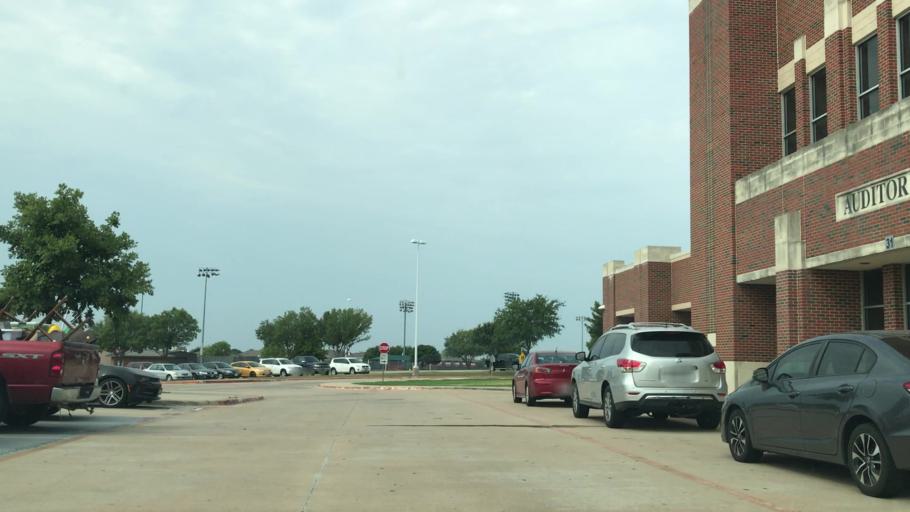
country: US
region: Texas
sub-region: Tarrant County
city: Keller
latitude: 32.9096
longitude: -97.2698
